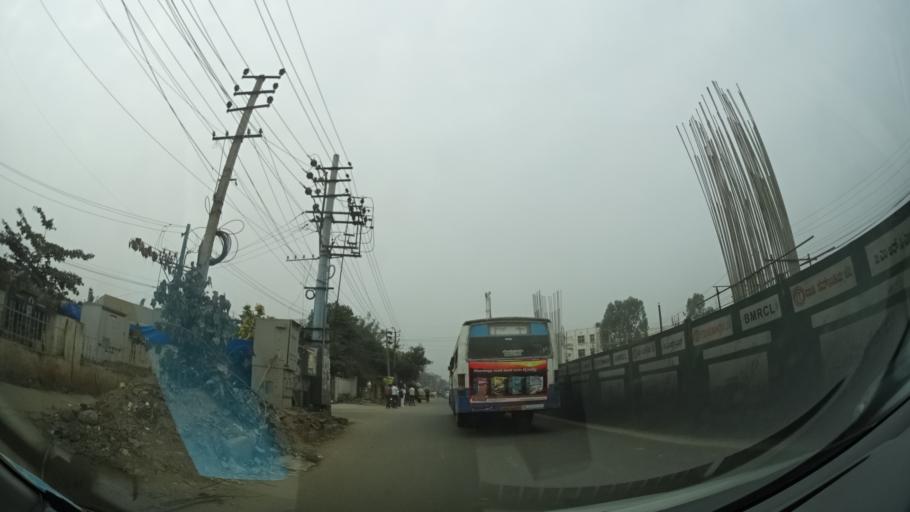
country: IN
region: Karnataka
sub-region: Bangalore Rural
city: Hoskote
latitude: 12.9896
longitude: 77.7129
